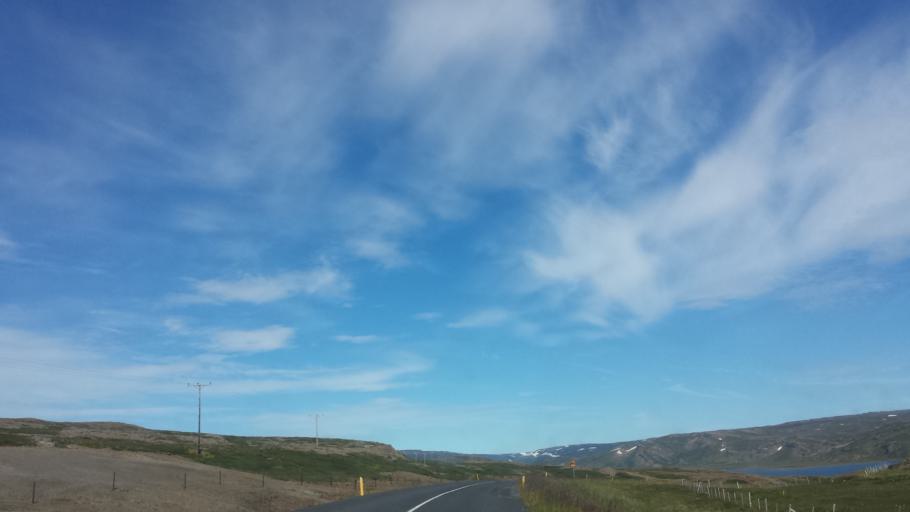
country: IS
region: West
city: Stykkisholmur
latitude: 65.7411
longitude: -21.7080
